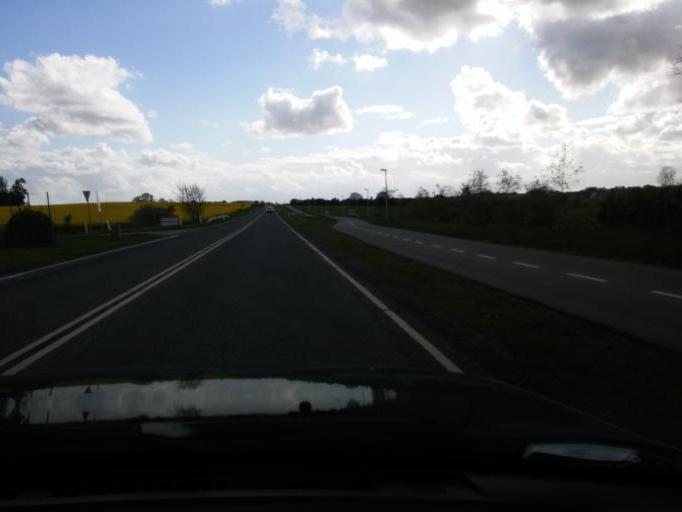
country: DK
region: South Denmark
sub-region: Faaborg-Midtfyn Kommune
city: Ringe
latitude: 55.2434
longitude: 10.5068
